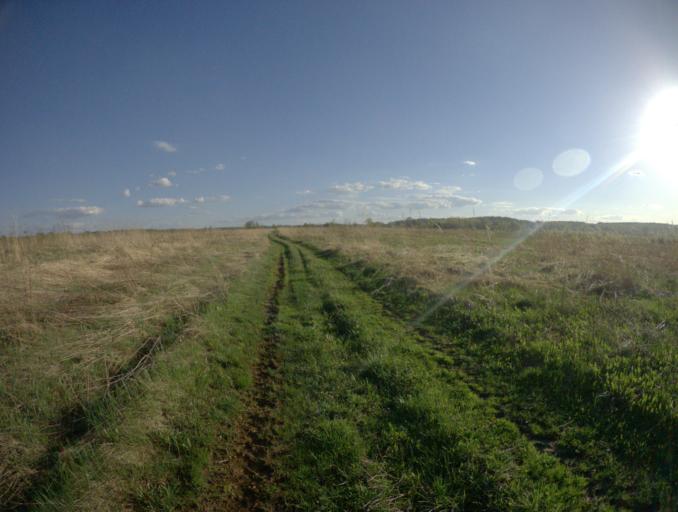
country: RU
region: Vladimir
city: Raduzhnyy
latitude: 56.0094
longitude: 40.2257
